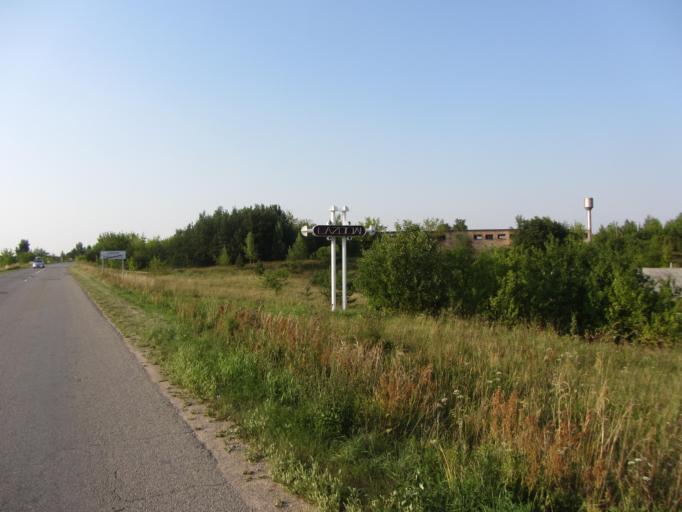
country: LT
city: Lazdijai
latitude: 54.2091
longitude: 23.5087
